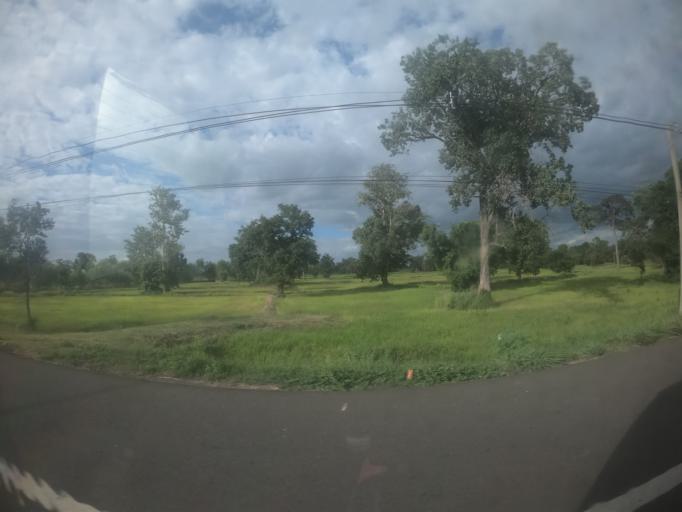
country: TH
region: Surin
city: Prasat
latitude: 14.5817
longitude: 103.4761
